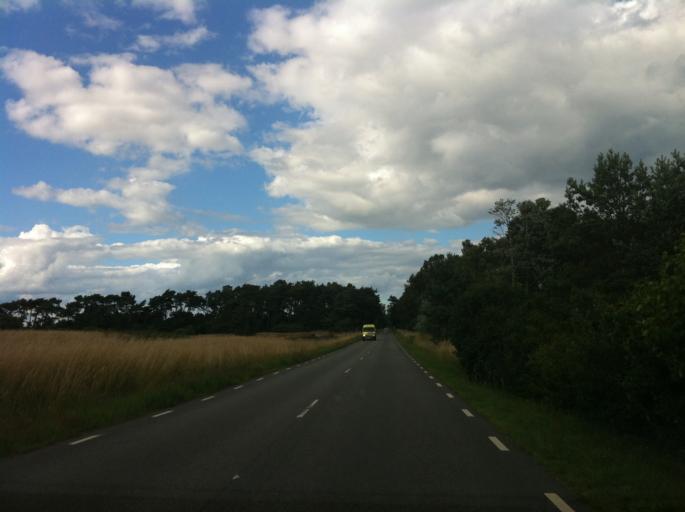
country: SE
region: Skane
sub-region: Simrishamns Kommun
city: Simrishamn
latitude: 55.4061
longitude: 14.1878
